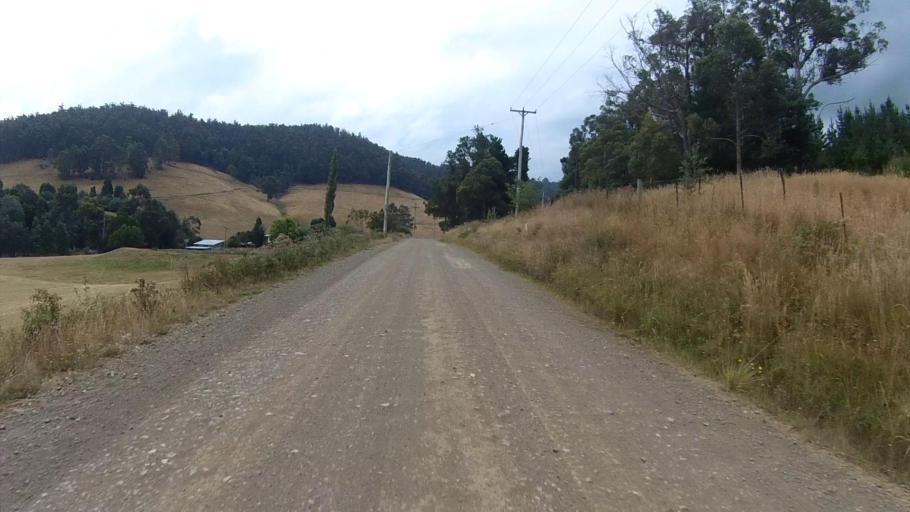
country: AU
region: Tasmania
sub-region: Huon Valley
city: Huonville
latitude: -42.9726
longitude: 147.0542
